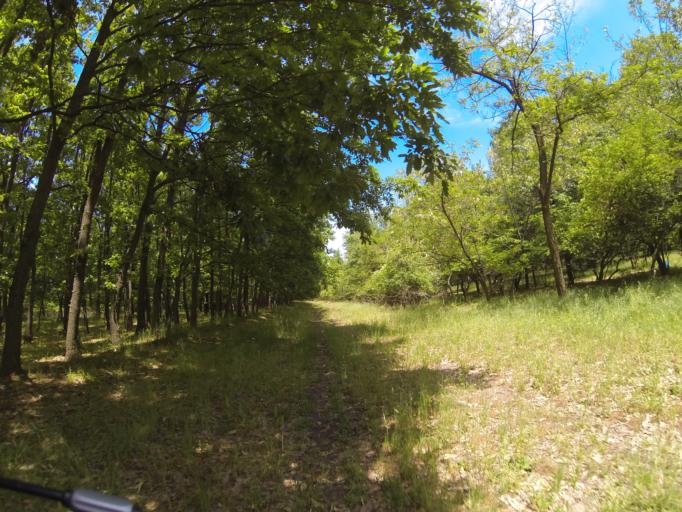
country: RO
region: Dolj
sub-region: Comuna Teslui
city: Teslui
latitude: 44.1679
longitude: 24.1649
